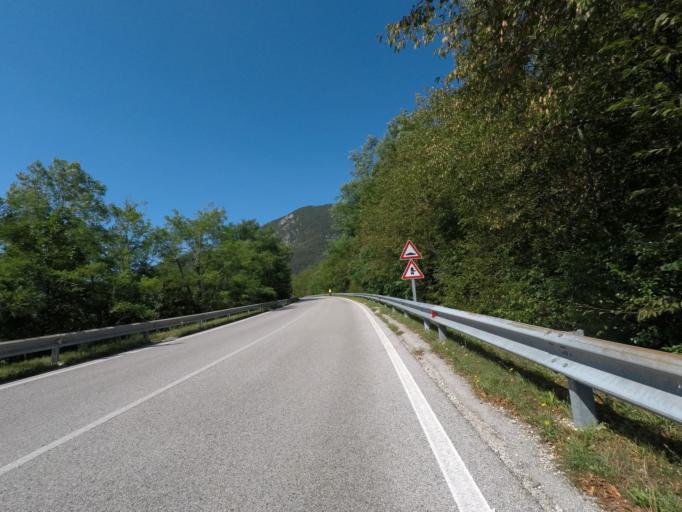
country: IT
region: Friuli Venezia Giulia
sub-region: Provincia di Udine
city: Trasaghis
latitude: 46.2670
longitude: 13.0478
